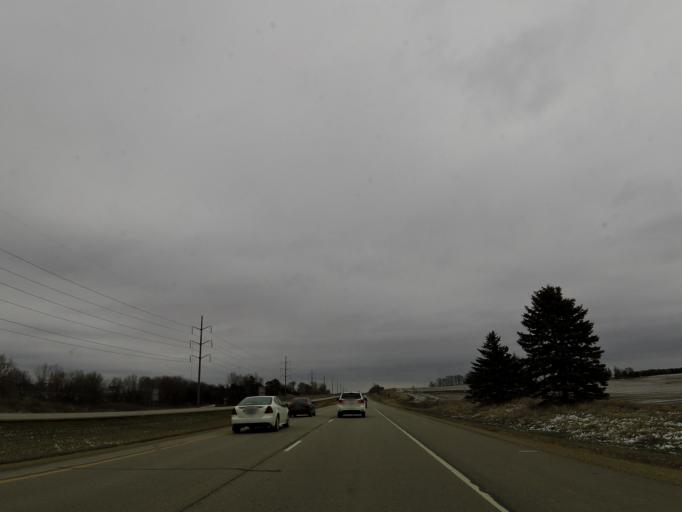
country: US
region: Minnesota
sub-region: Olmsted County
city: Byron
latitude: 44.0288
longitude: -92.6200
